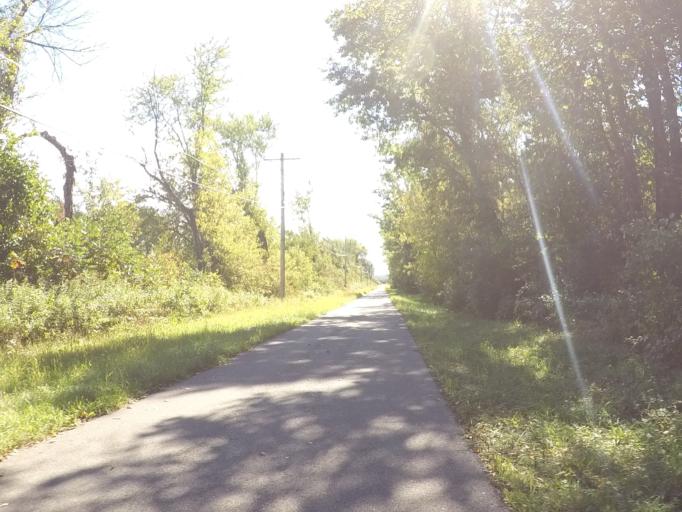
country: US
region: Wisconsin
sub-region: Richland County
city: Richland Center
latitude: 43.3152
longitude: -90.3579
